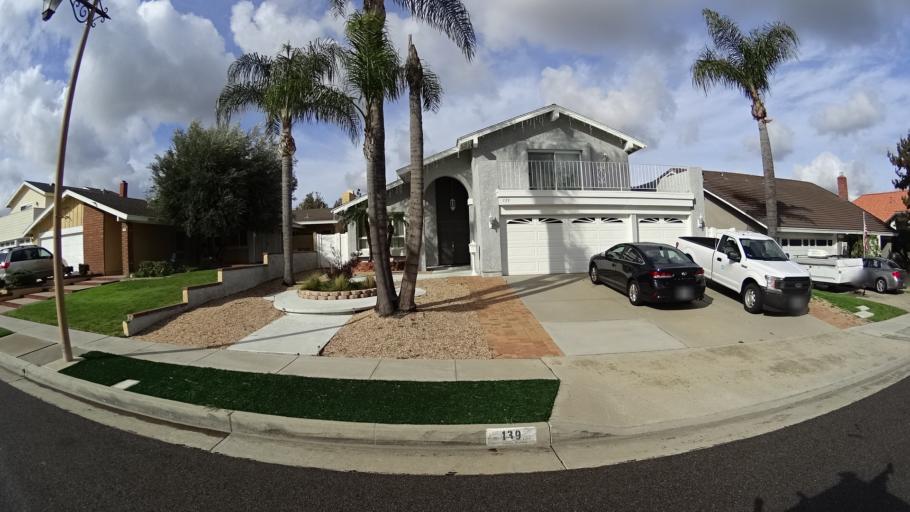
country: US
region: California
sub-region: Orange County
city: Villa Park
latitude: 33.8511
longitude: -117.7822
